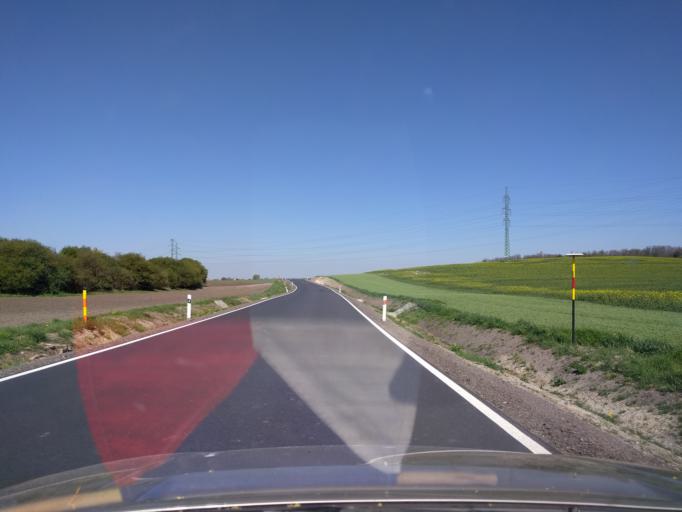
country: CZ
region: Central Bohemia
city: Cesky Brod
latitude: 50.1209
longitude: 14.8563
